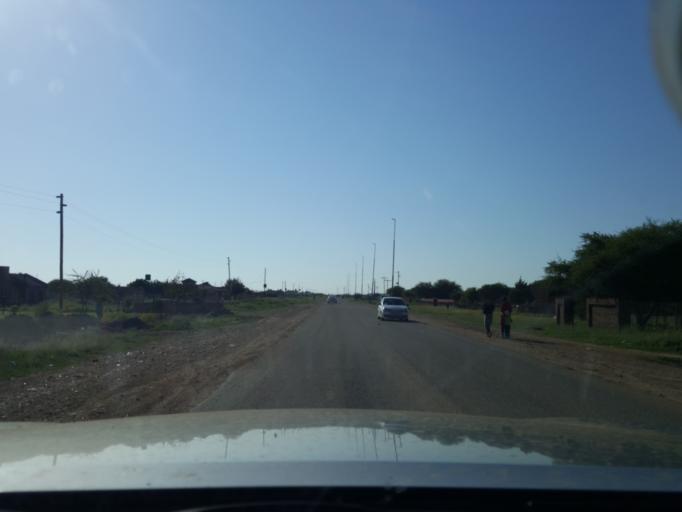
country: ZA
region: North-West
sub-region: Ngaka Modiri Molema District Municipality
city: Mmabatho
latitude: -25.8347
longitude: 25.6635
